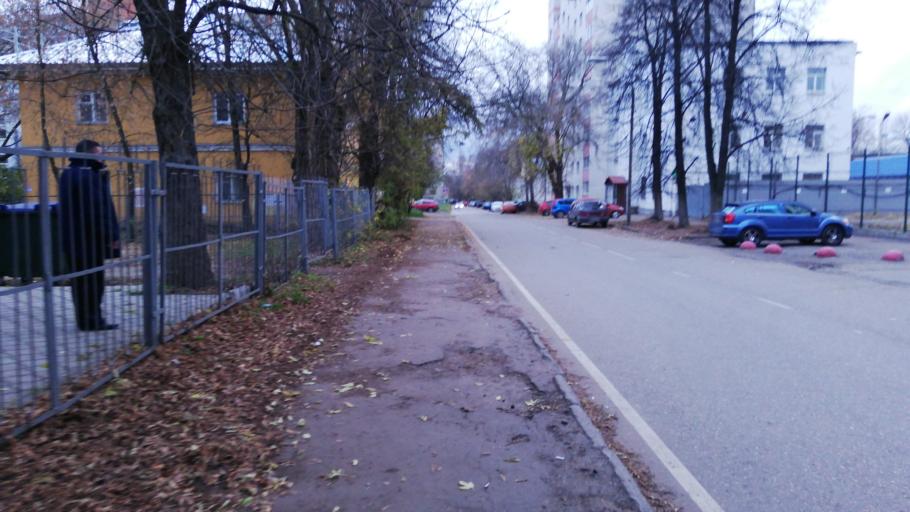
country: RU
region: Jaroslavl
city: Yaroslavl
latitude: 57.6258
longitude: 39.8441
